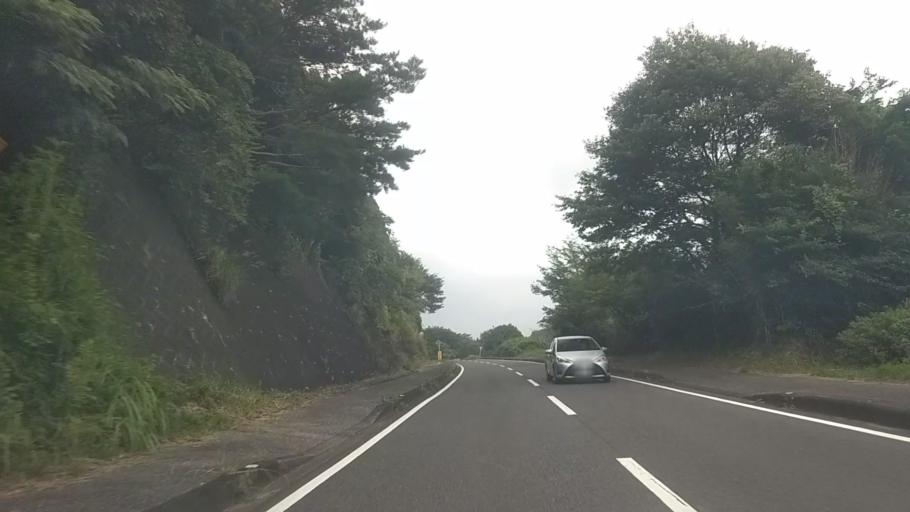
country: JP
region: Chiba
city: Kawaguchi
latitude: 35.2417
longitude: 140.0833
